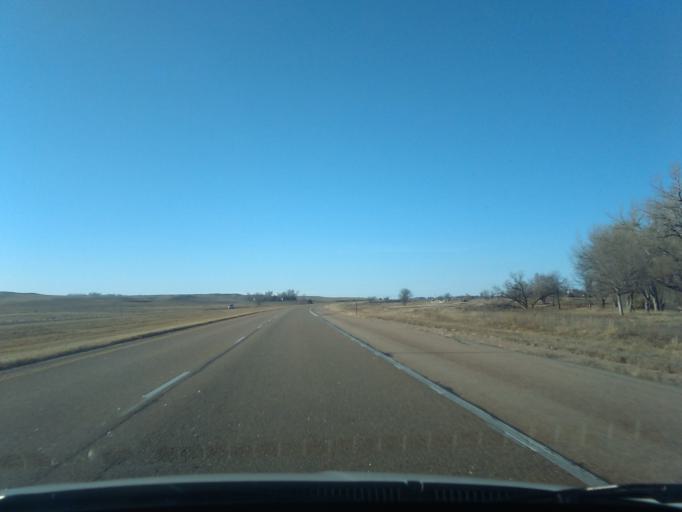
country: US
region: Nebraska
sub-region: Deuel County
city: Chappell
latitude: 41.0587
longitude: -102.4333
